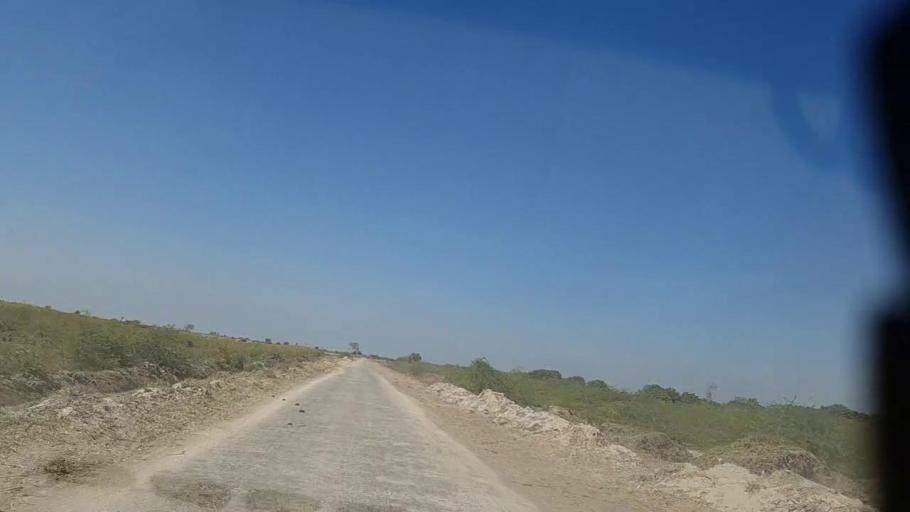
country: PK
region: Sindh
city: Mirwah Gorchani
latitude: 25.2234
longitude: 69.0224
